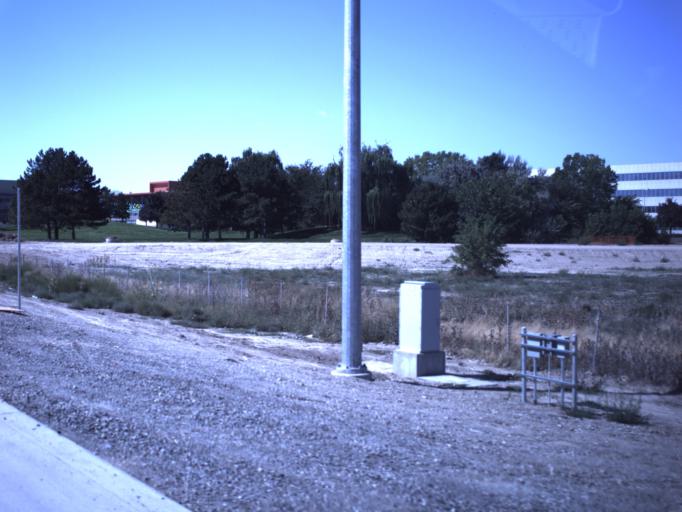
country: US
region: Utah
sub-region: Salt Lake County
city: Taylorsville
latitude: 40.6773
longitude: -111.9525
